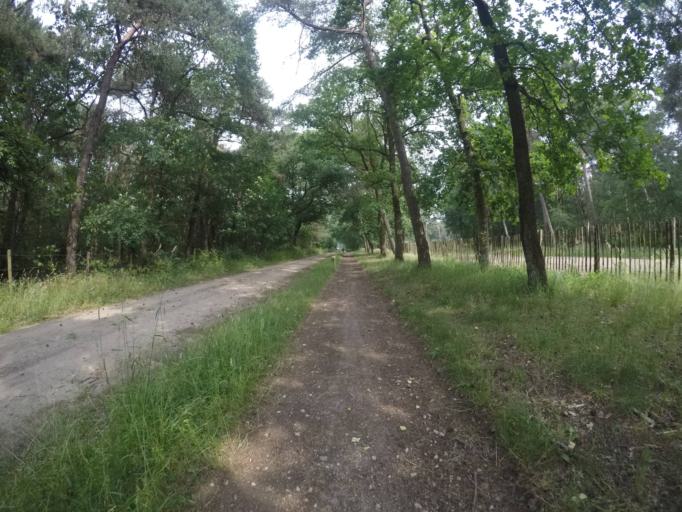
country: NL
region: Gelderland
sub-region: Oost Gelre
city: Lichtenvoorde
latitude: 52.0027
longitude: 6.6035
